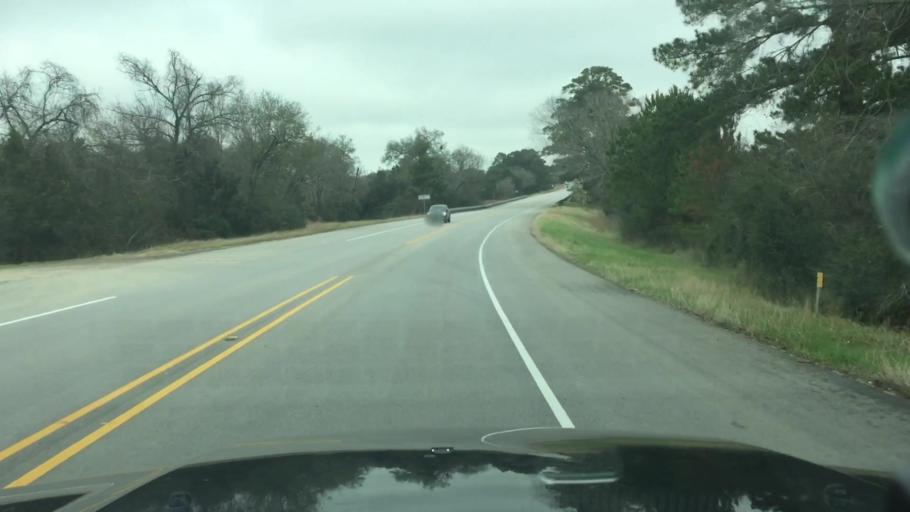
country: US
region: Texas
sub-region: Lee County
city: Giddings
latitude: 30.0826
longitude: -96.9170
